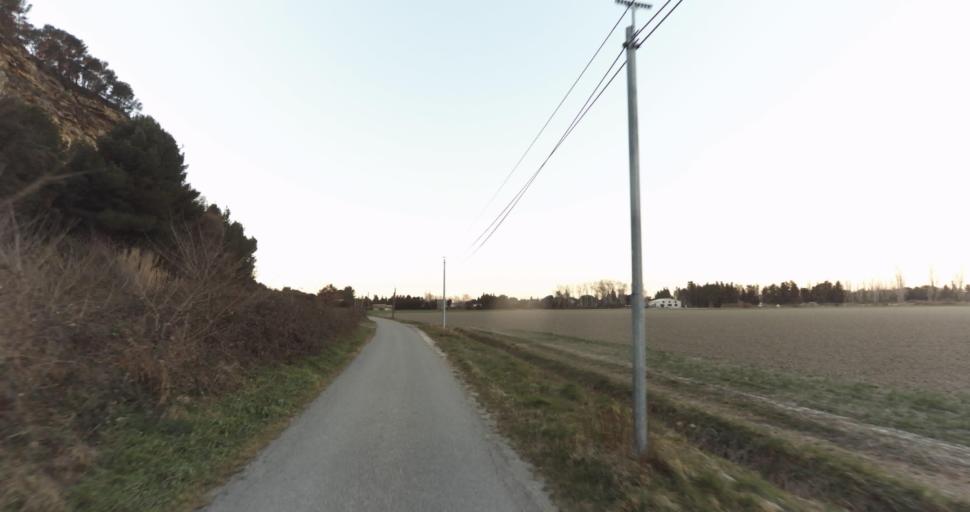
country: FR
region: Provence-Alpes-Cote d'Azur
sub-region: Departement des Bouches-du-Rhone
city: Barbentane
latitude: 43.8931
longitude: 4.7670
